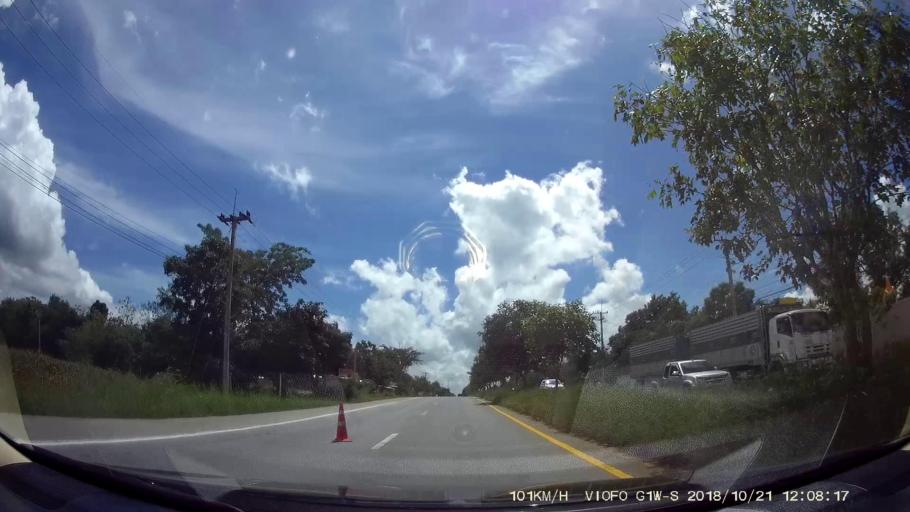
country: TH
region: Chaiyaphum
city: Chatturat
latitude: 15.4359
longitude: 101.8302
